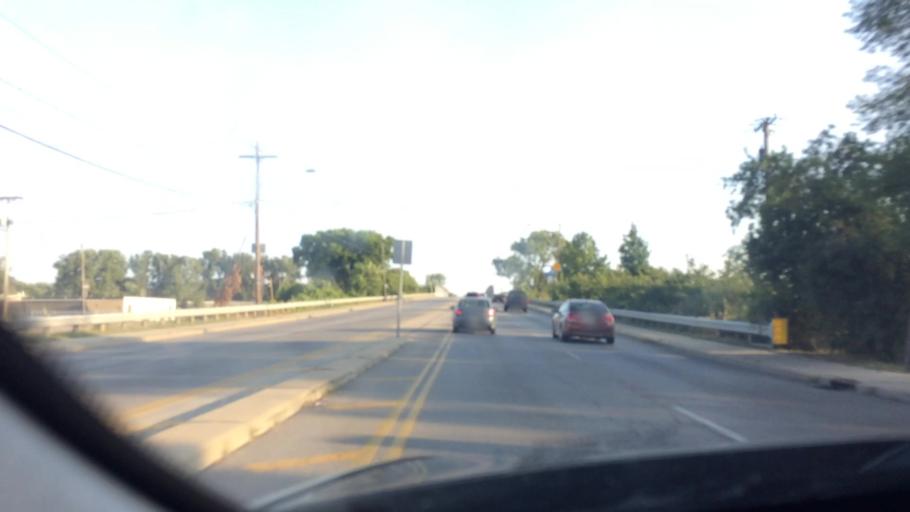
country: US
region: Ohio
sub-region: Lucas County
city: Ottawa Hills
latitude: 41.6346
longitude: -83.6259
